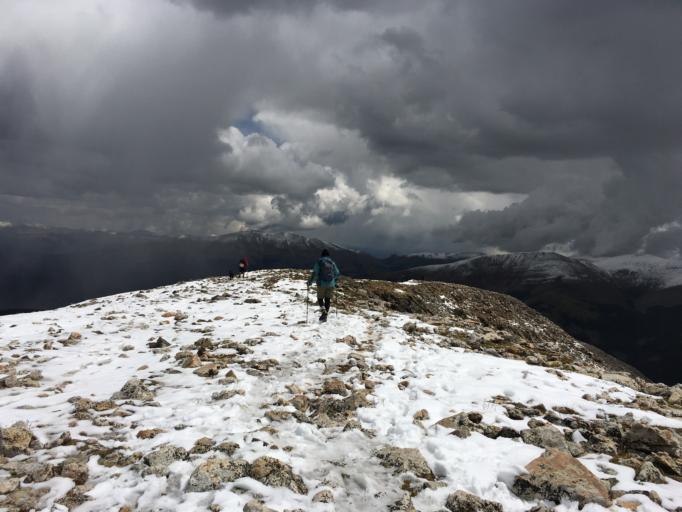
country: US
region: Colorado
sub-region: Summit County
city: Breckenridge
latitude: 39.3948
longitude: -106.0929
